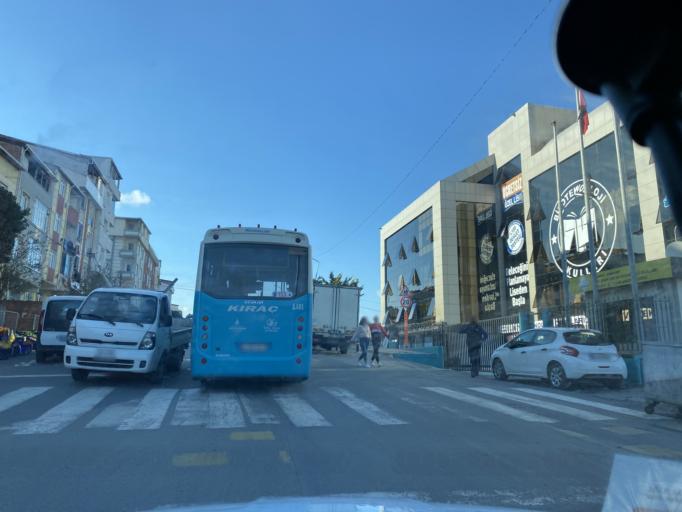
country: TR
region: Istanbul
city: Esenyurt
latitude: 41.0469
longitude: 28.6485
